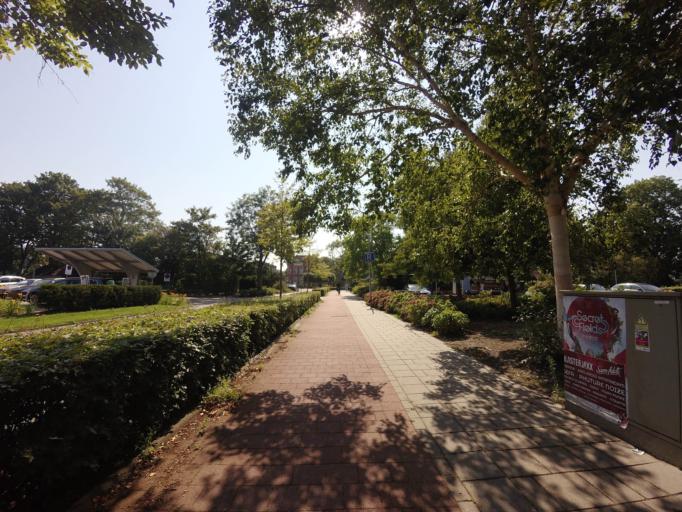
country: NL
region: Groningen
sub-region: Gemeente Zuidhorn
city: Grijpskerk
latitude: 53.2647
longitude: 6.3063
